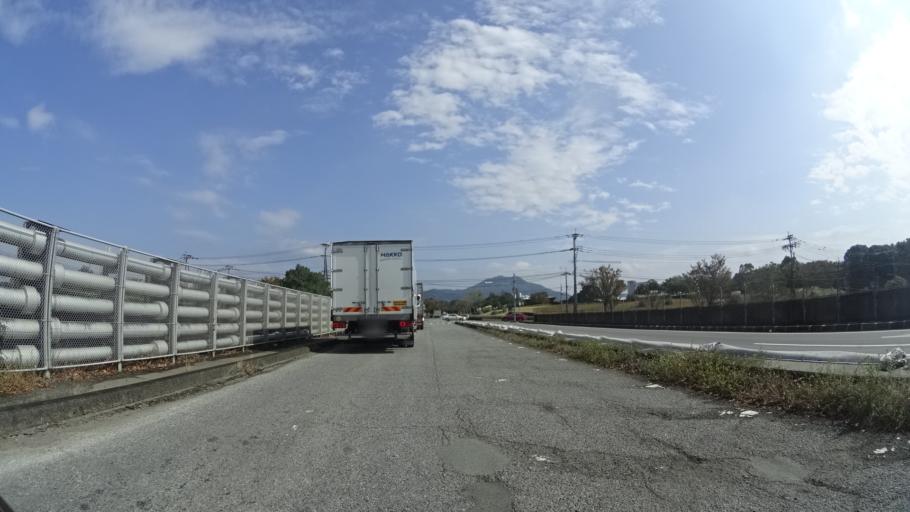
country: JP
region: Kumamoto
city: Kumamoto
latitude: 32.7485
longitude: 130.7873
